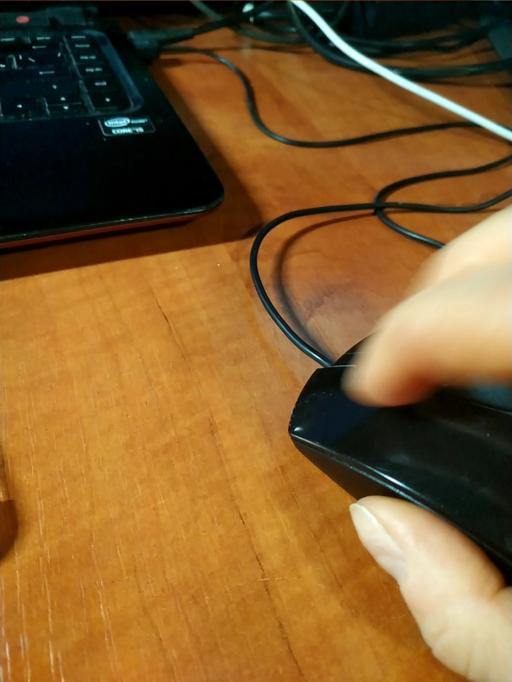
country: RU
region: Kaluga
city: Iznoski
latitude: 54.9356
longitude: 35.4122
